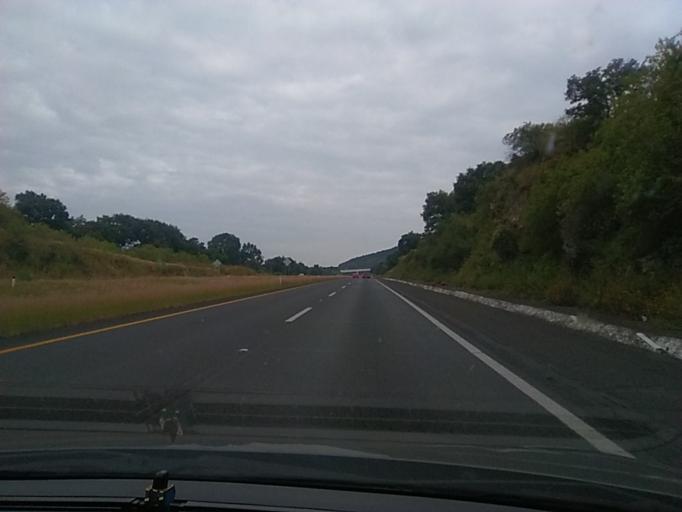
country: MX
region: Michoacan
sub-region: Puruandiro
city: San Lorenzo
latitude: 19.9652
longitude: -101.6987
